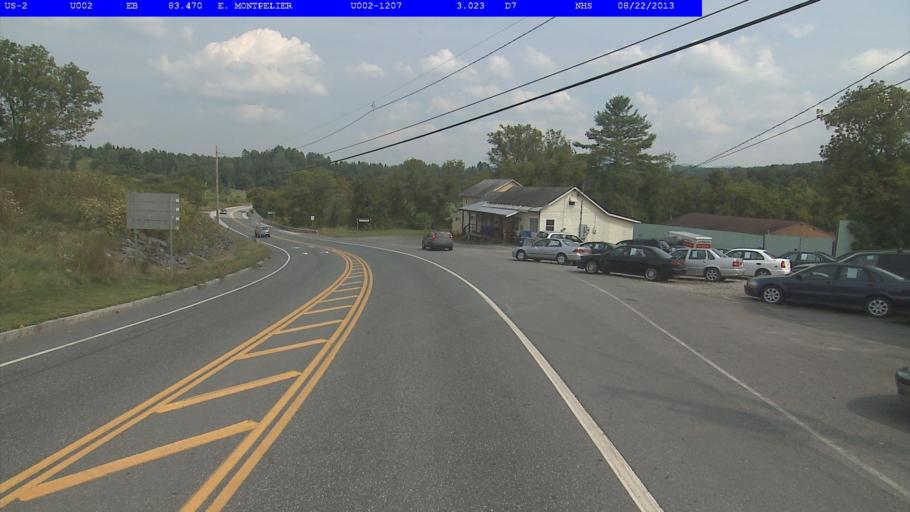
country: US
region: Vermont
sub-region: Washington County
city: Barre
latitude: 44.2713
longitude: -72.4851
